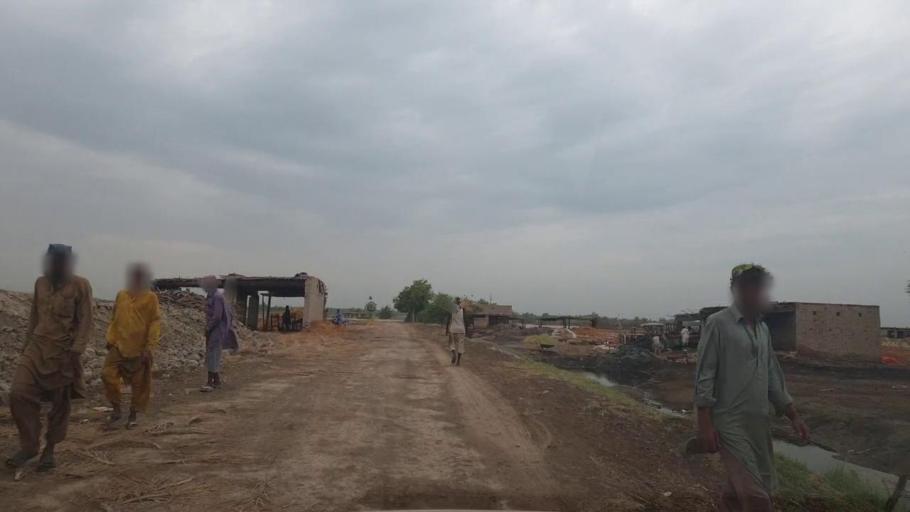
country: PK
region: Sindh
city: Khairpur
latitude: 27.5907
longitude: 68.8132
